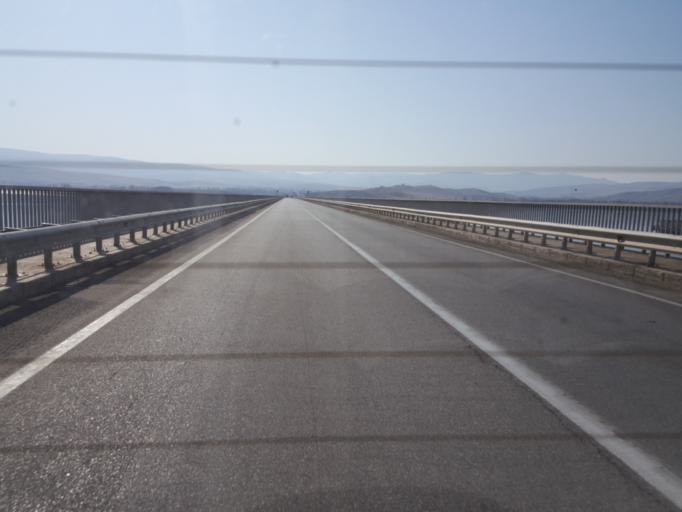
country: TR
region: Corum
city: Iskilip
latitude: 40.6271
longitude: 34.5657
